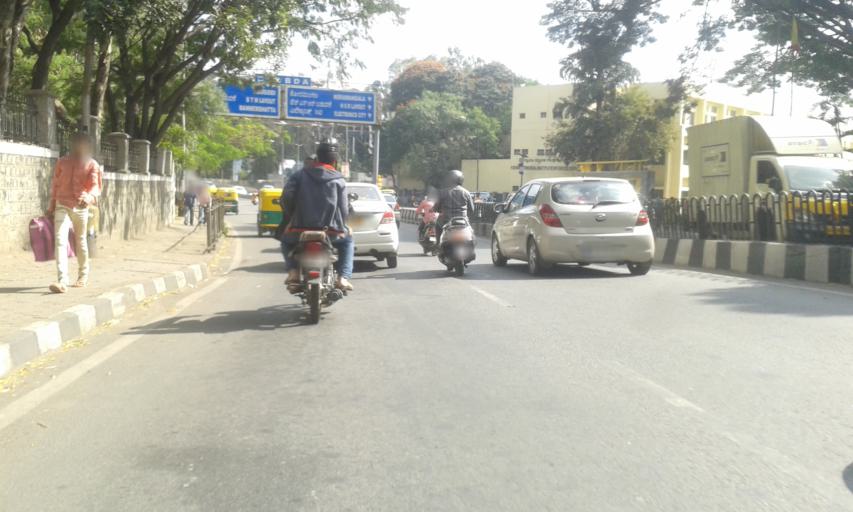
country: IN
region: Karnataka
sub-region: Bangalore Urban
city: Bangalore
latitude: 12.9388
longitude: 77.5984
